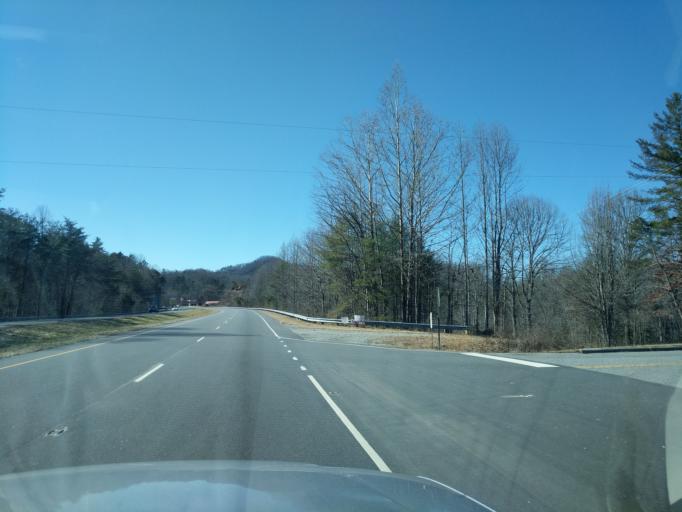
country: US
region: North Carolina
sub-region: Swain County
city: Bryson City
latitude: 35.3866
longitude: -83.4878
